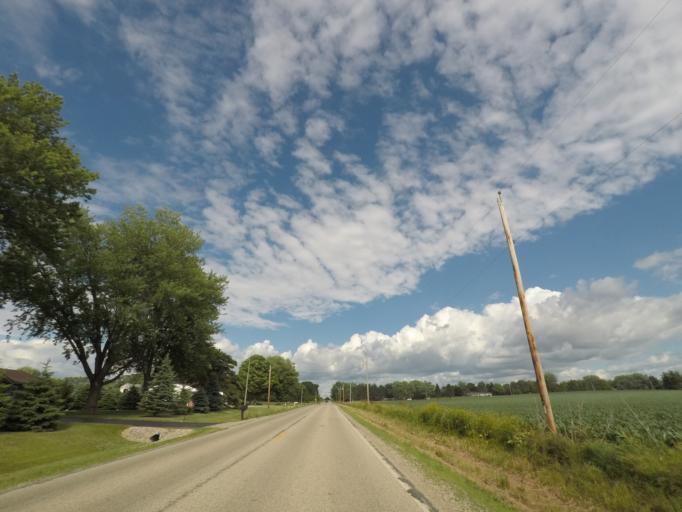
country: US
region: Wisconsin
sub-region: Rock County
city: Janesville
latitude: 42.7010
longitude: -89.0758
